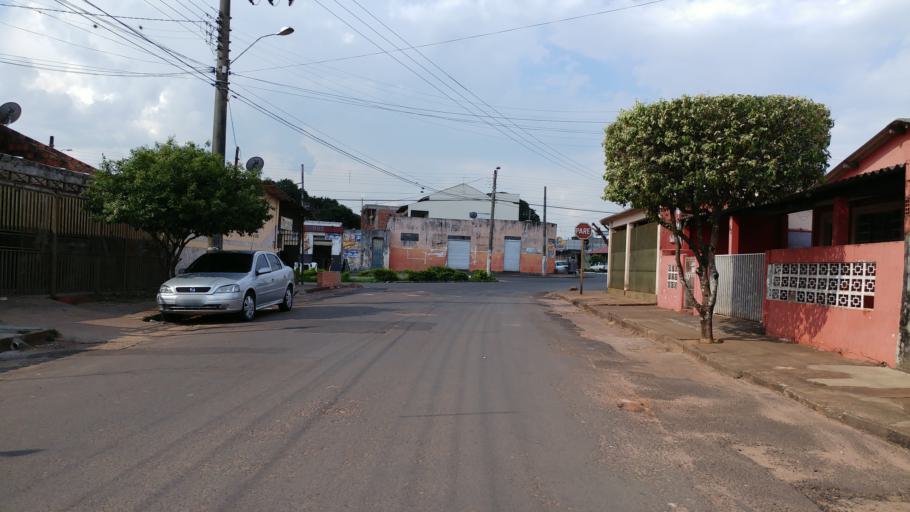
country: BR
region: Sao Paulo
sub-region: Paraguacu Paulista
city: Paraguacu Paulista
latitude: -22.4215
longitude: -50.5860
